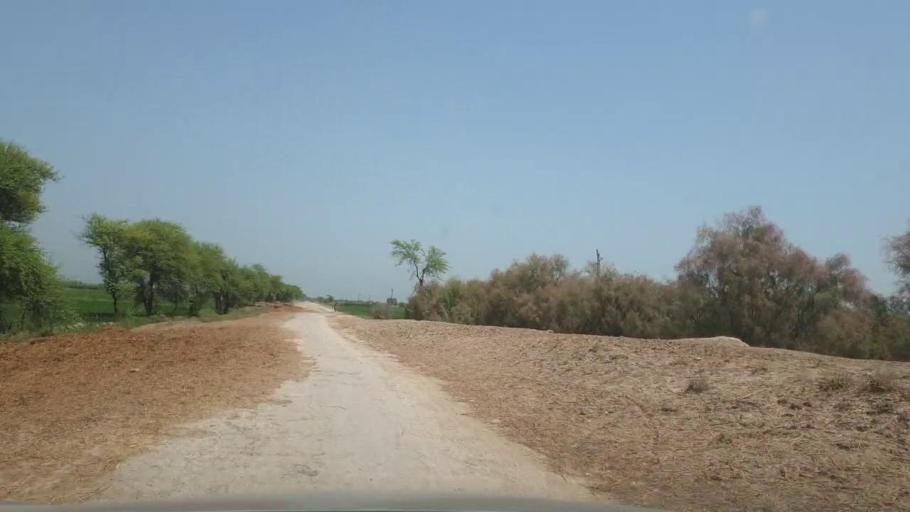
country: PK
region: Sindh
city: Warah
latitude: 27.5092
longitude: 67.7796
